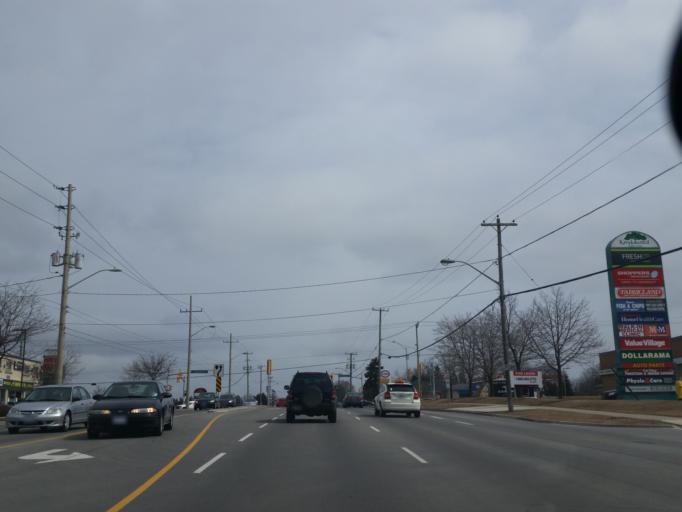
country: CA
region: Ontario
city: Oshawa
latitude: 43.8884
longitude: -78.9045
